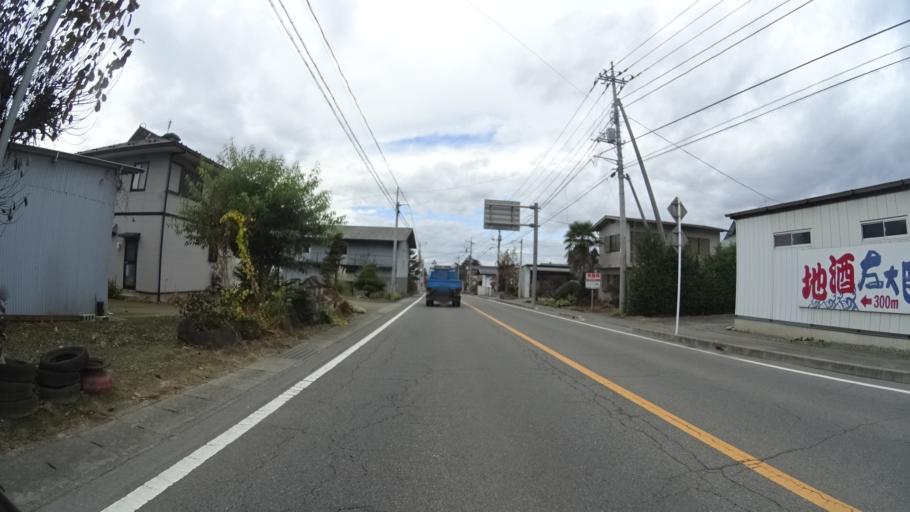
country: JP
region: Gunma
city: Numata
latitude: 36.6637
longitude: 139.1436
